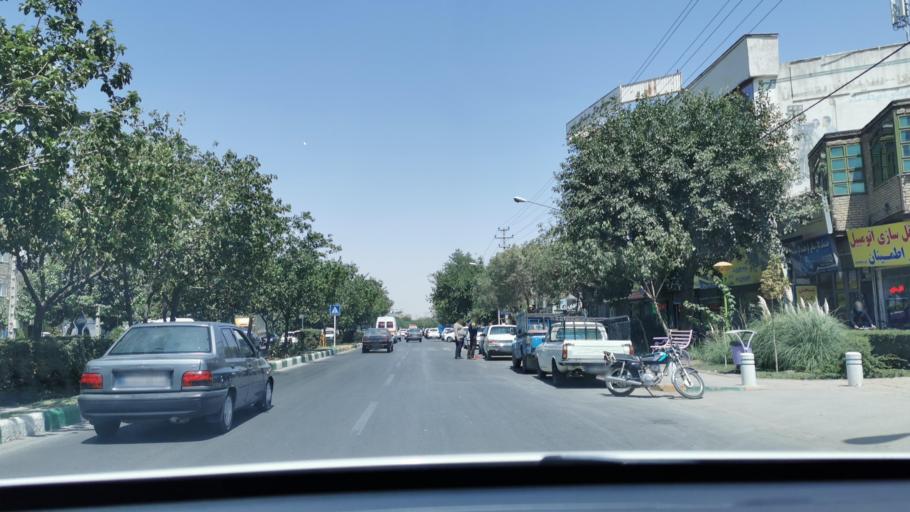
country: IR
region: Razavi Khorasan
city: Mashhad
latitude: 36.3446
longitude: 59.6261
